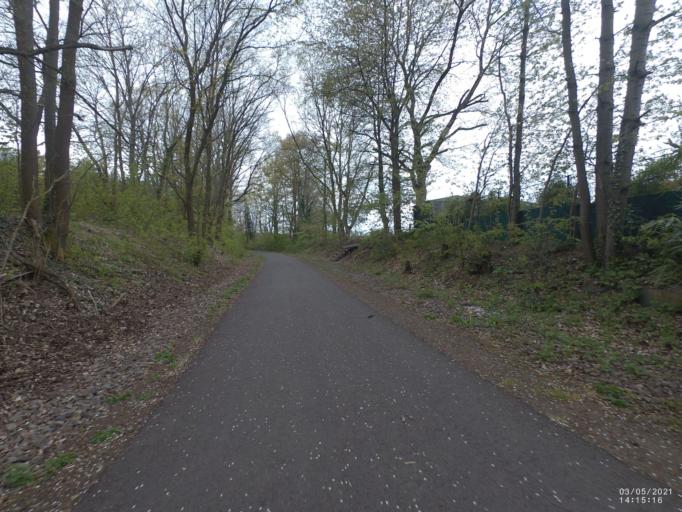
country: DE
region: Rheinland-Pfalz
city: Bassenheim
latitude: 50.3578
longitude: 7.4691
